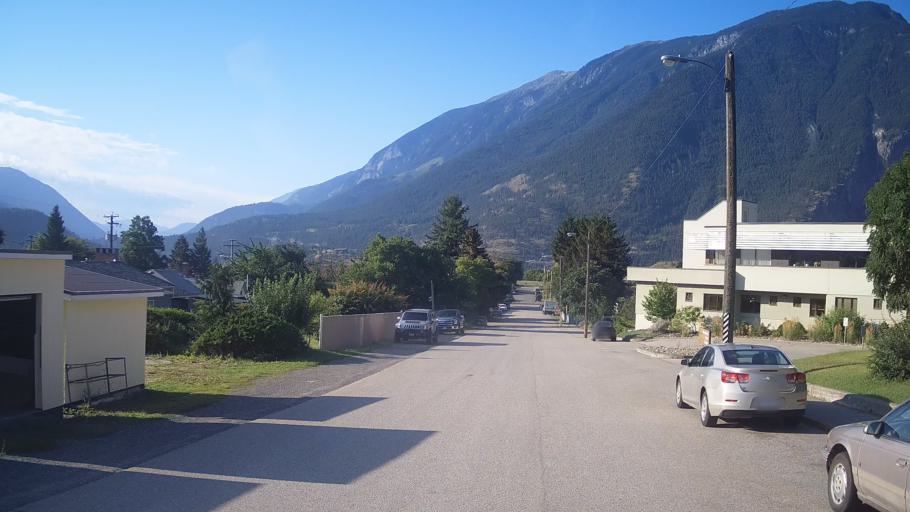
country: CA
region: British Columbia
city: Lillooet
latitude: 50.6898
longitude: -121.9388
